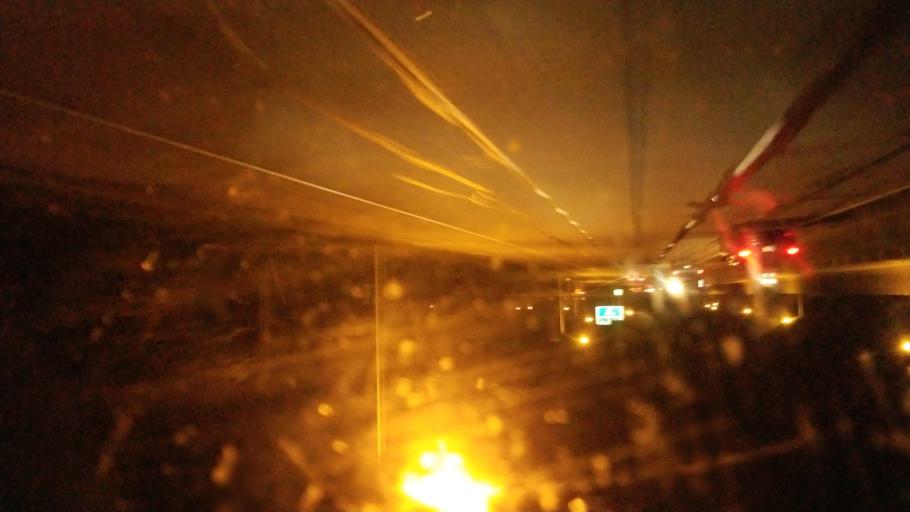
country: US
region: Indiana
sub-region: Allen County
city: Fort Wayne
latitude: 41.1941
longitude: -85.1038
